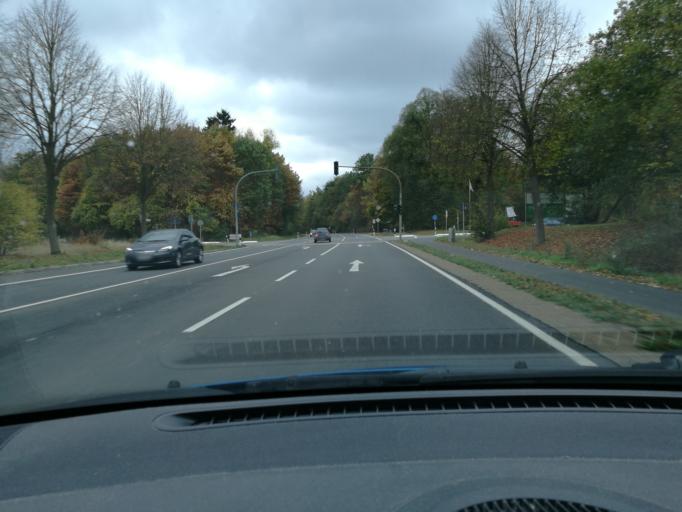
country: DE
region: Schleswig-Holstein
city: Fredeburg
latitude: 53.6734
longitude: 10.7258
